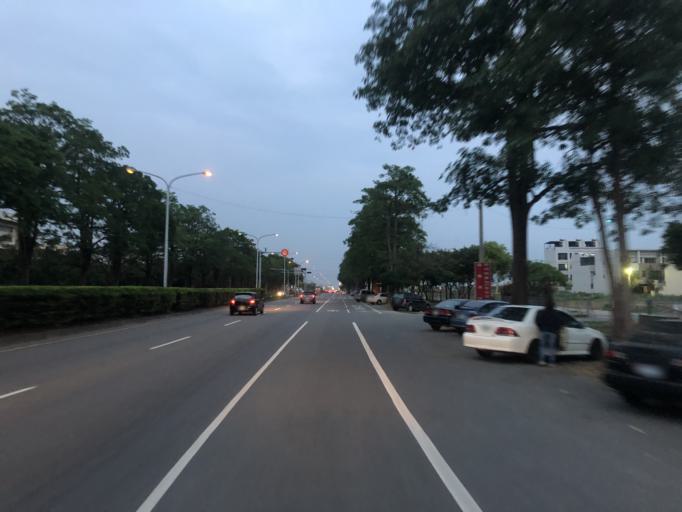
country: TW
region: Taiwan
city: Yujing
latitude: 23.1289
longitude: 120.3195
